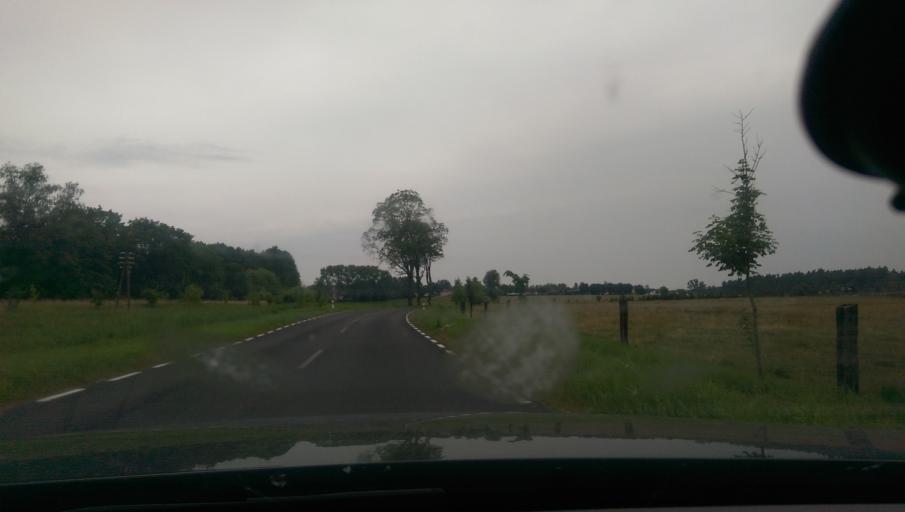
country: PL
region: Warmian-Masurian Voivodeship
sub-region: Powiat piski
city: Orzysz
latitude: 53.8101
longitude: 21.8498
